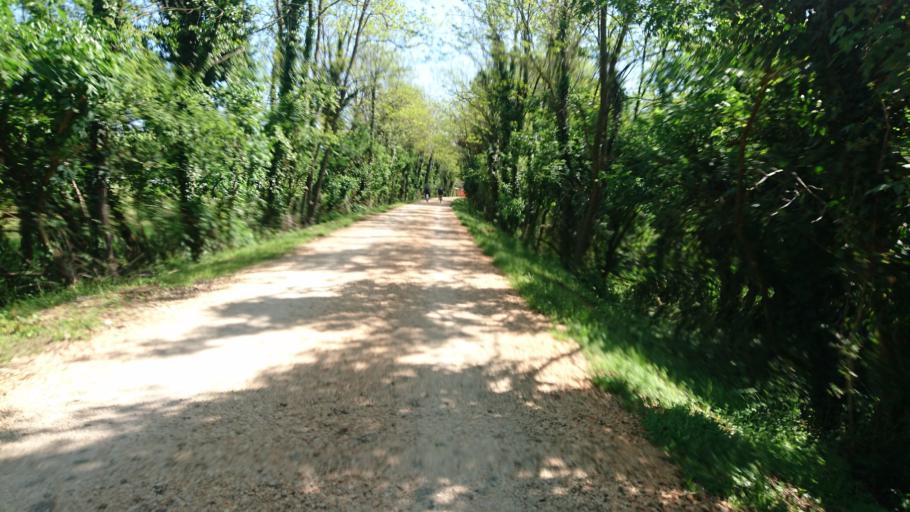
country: IT
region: Veneto
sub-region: Provincia di Treviso
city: Treviso
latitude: 45.6634
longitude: 12.2115
